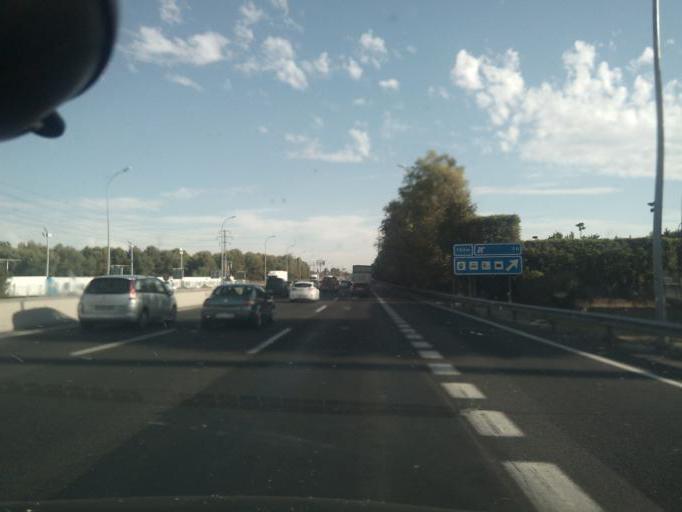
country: ES
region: Madrid
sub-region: Provincia de Madrid
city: Pinto
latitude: 40.2551
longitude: -3.6903
